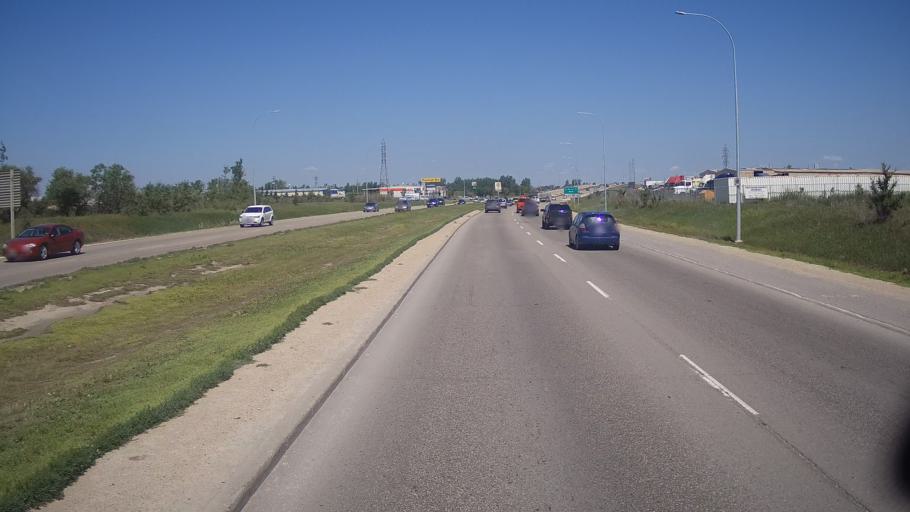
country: CA
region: Manitoba
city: Winnipeg
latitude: 49.8878
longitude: -97.0722
